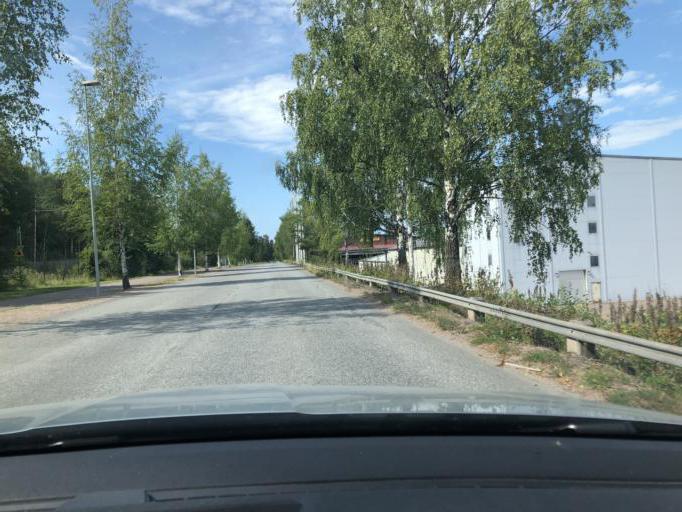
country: SE
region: Dalarna
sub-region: Avesta Kommun
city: Avesta
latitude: 60.1461
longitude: 16.1892
